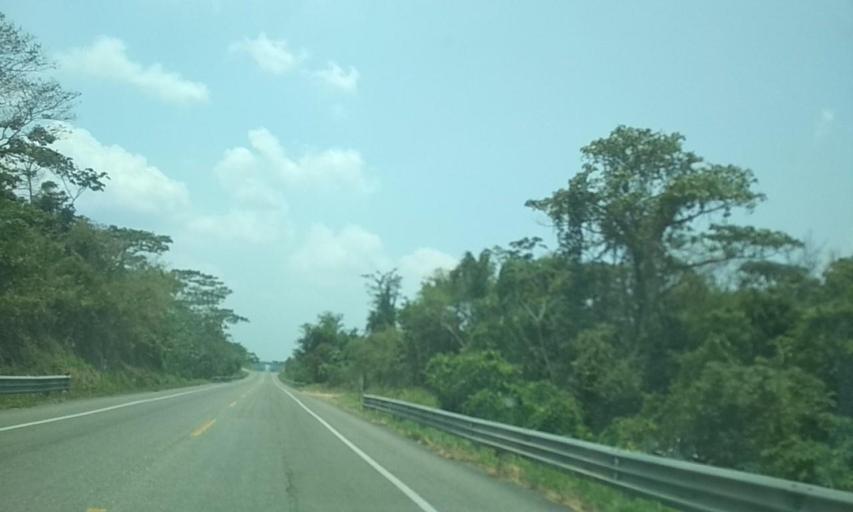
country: MX
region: Tabasco
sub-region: Huimanguillo
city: Francisco Rueda
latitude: 17.6661
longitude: -93.8626
